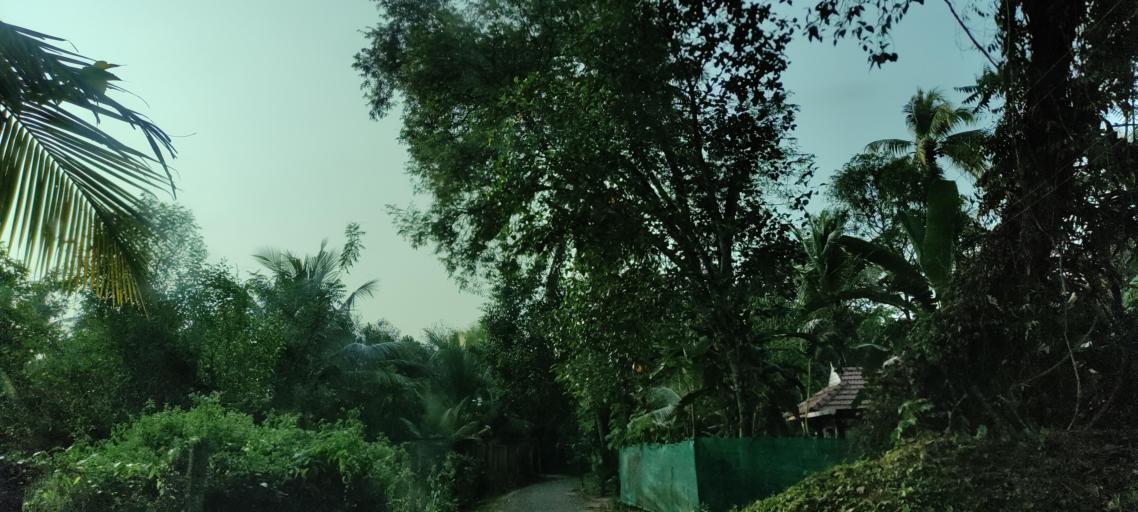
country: IN
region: Kerala
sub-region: Alappuzha
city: Shertallai
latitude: 9.6686
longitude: 76.3563
